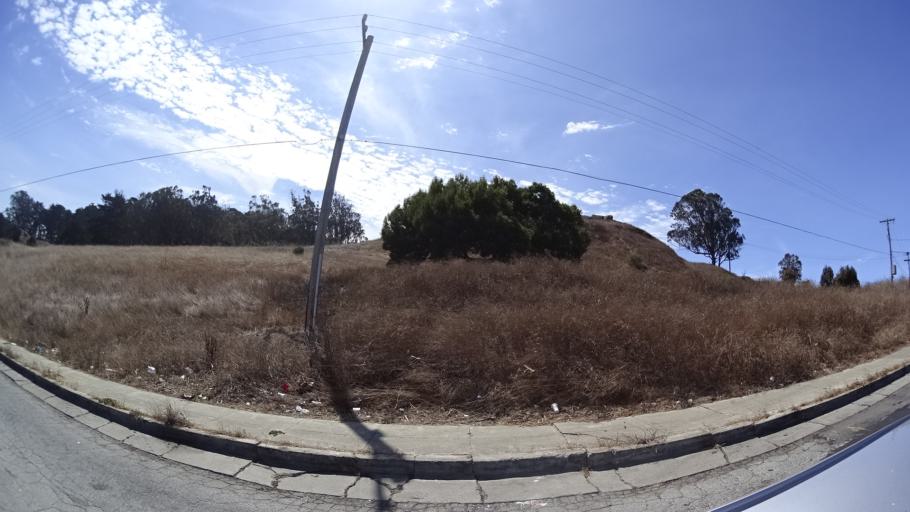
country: US
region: California
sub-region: San Mateo County
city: Daly City
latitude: 37.7146
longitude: -122.4249
